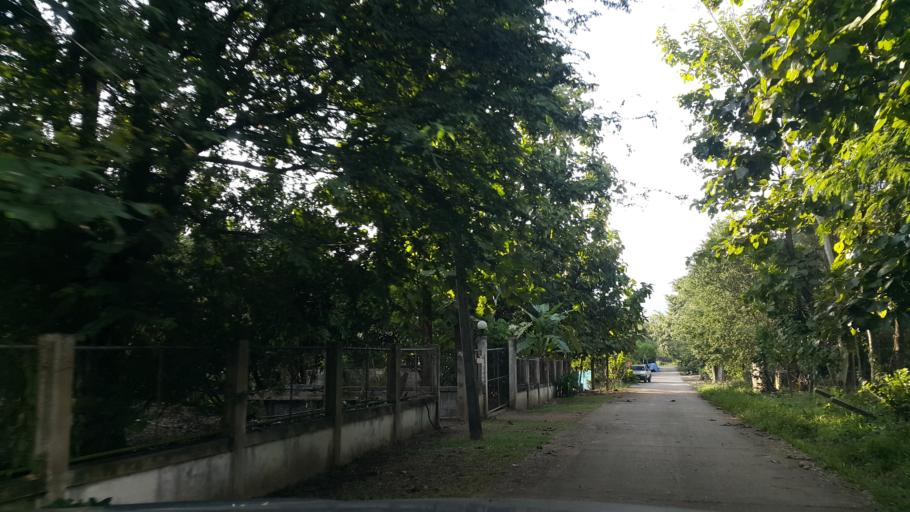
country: TH
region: Chiang Mai
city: Mae On
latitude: 18.7395
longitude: 99.2380
